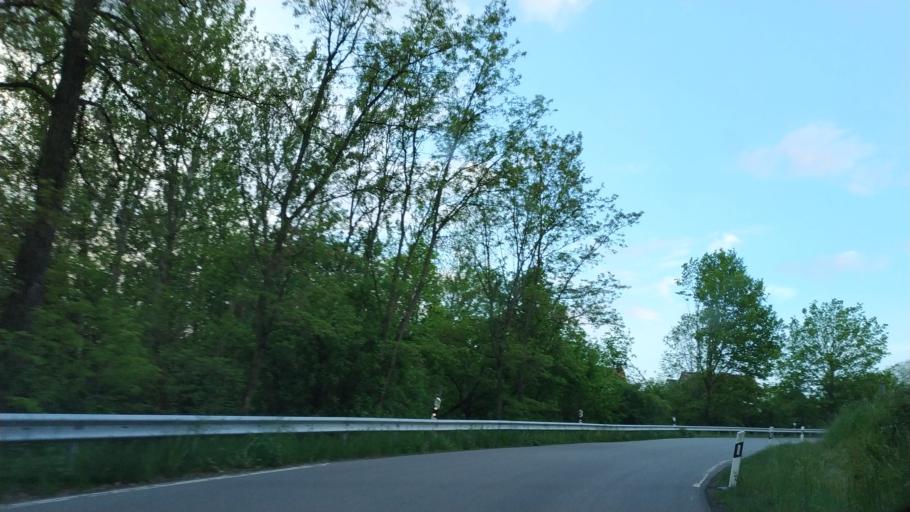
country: DE
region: Saxony
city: Stadt Wehlen
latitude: 50.9596
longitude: 14.0242
